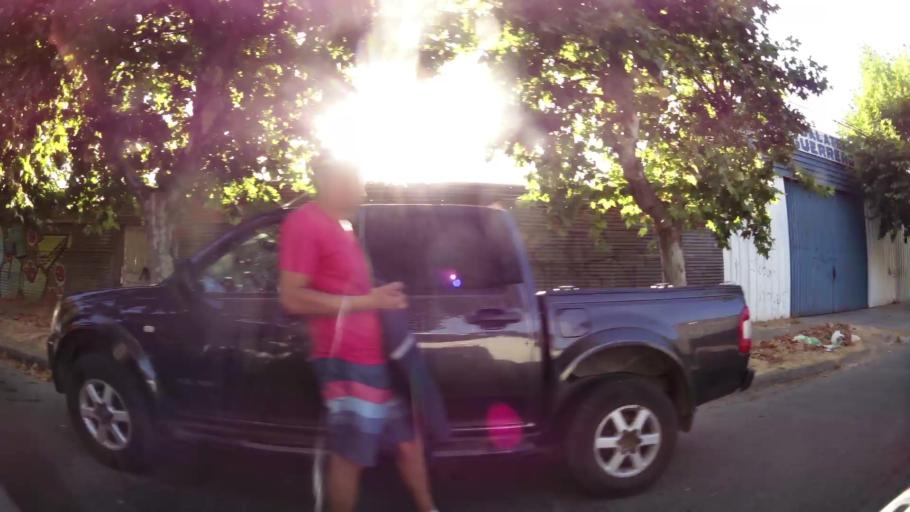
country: CL
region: Maule
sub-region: Provincia de Talca
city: Talca
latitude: -35.4160
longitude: -71.6601
